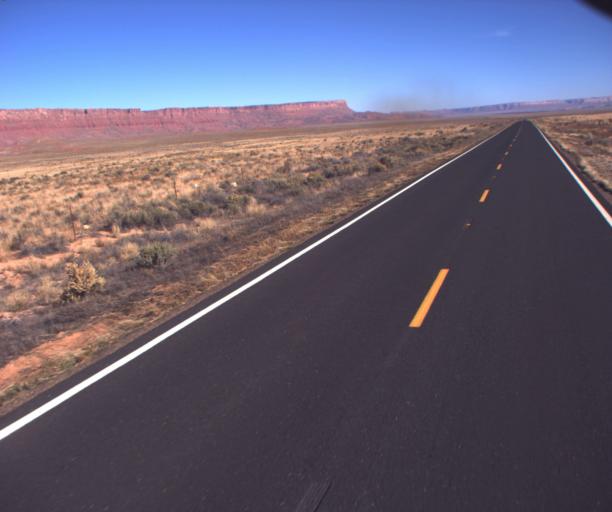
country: US
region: Arizona
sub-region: Coconino County
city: Fredonia
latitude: 36.7225
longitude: -112.0178
